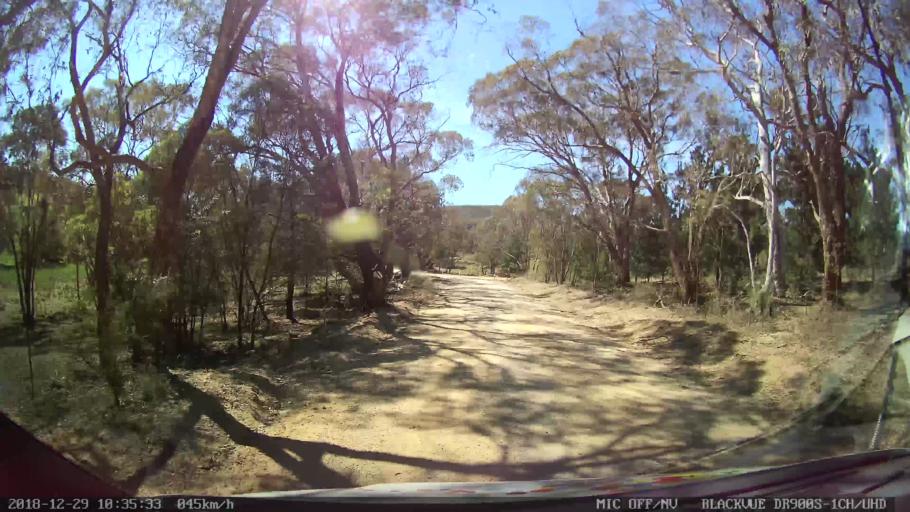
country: AU
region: New South Wales
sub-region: Yass Valley
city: Gundaroo
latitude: -34.9920
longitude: 149.4838
